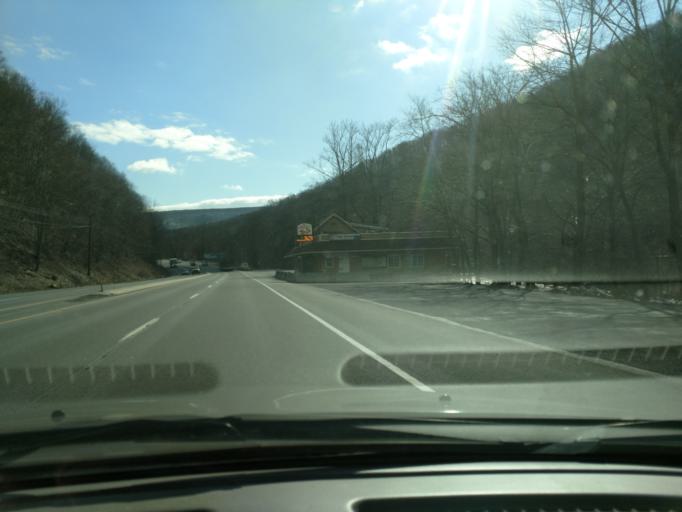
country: US
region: Pennsylvania
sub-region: Berks County
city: West Hamburg
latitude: 40.5936
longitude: -76.0269
